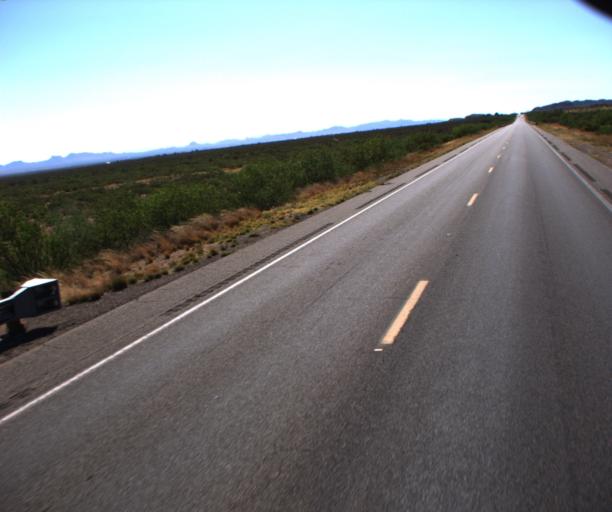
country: US
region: Arizona
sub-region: Cochise County
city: Bisbee
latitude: 31.4099
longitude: -109.7864
